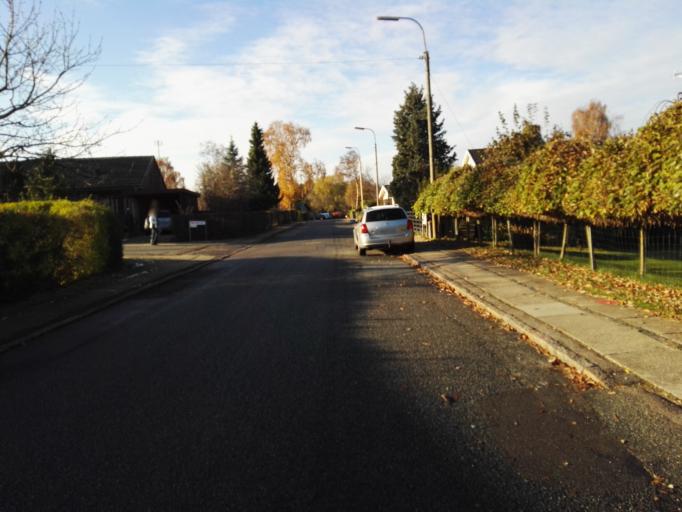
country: DK
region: Capital Region
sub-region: Herlev Kommune
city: Herlev
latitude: 55.7287
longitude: 12.4096
